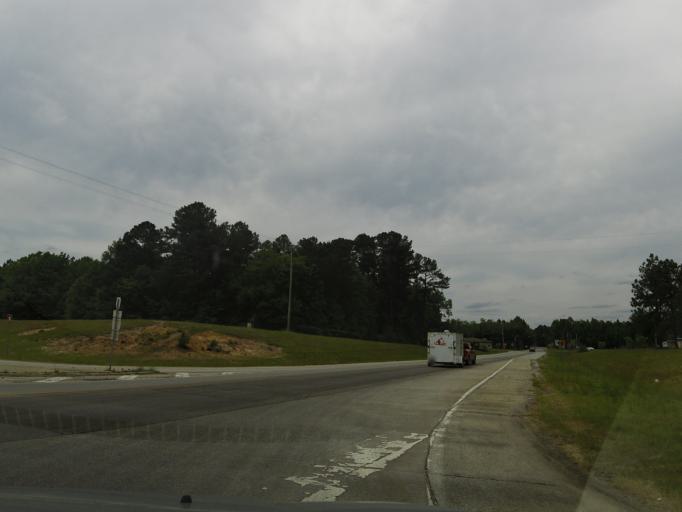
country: US
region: Georgia
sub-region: Candler County
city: Metter
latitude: 32.3755
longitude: -82.1661
